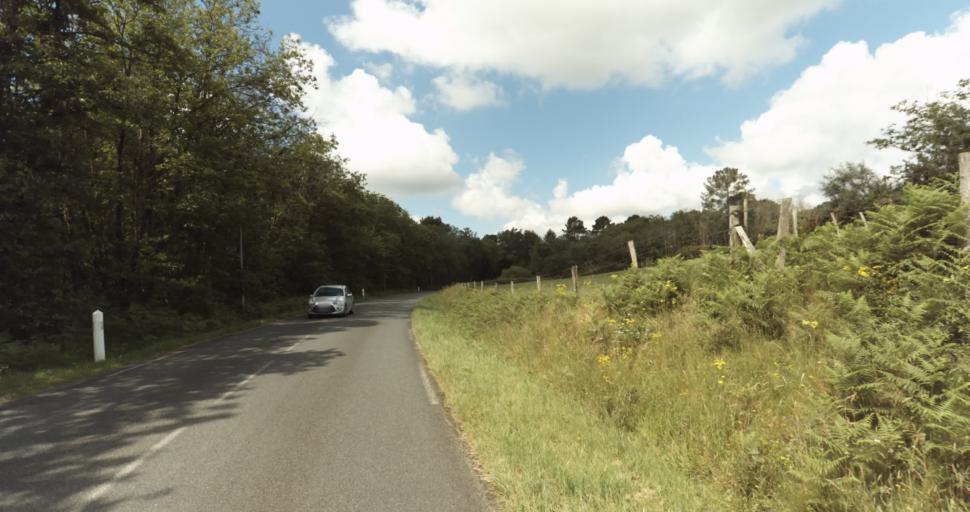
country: FR
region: Aquitaine
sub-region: Departement de la Dordogne
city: Beaumont-du-Perigord
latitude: 44.7870
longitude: 0.8399
